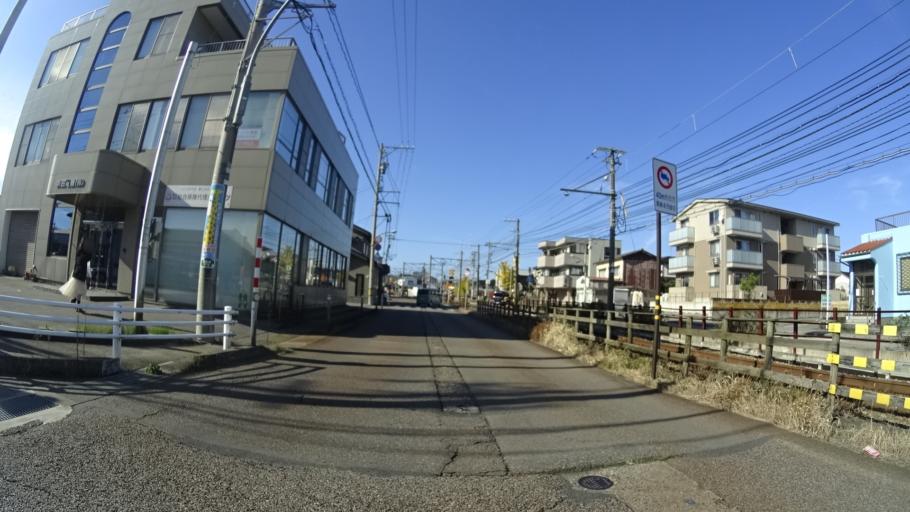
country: JP
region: Ishikawa
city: Kanazawa-shi
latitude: 36.6324
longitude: 136.6356
